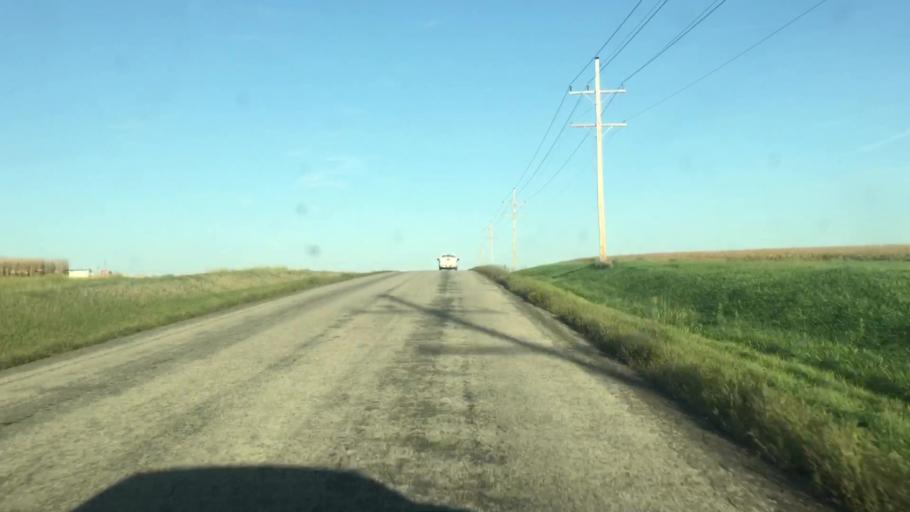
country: US
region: Kansas
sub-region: Brown County
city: Horton
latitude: 39.5657
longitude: -95.3943
